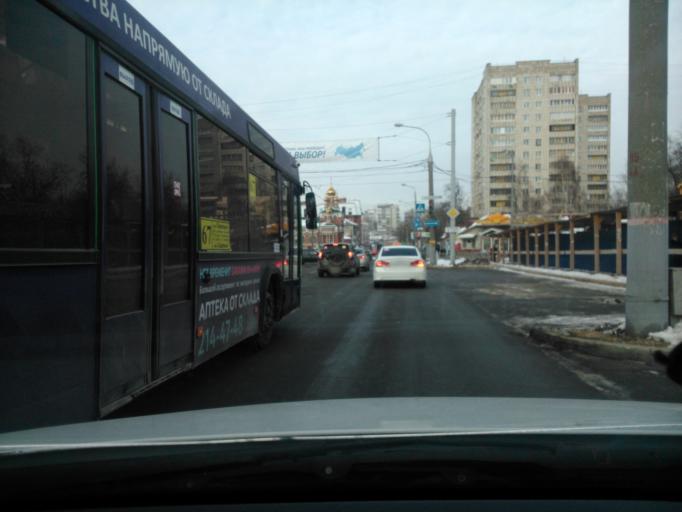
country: RU
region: Perm
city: Perm
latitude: 58.0035
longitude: 56.2230
